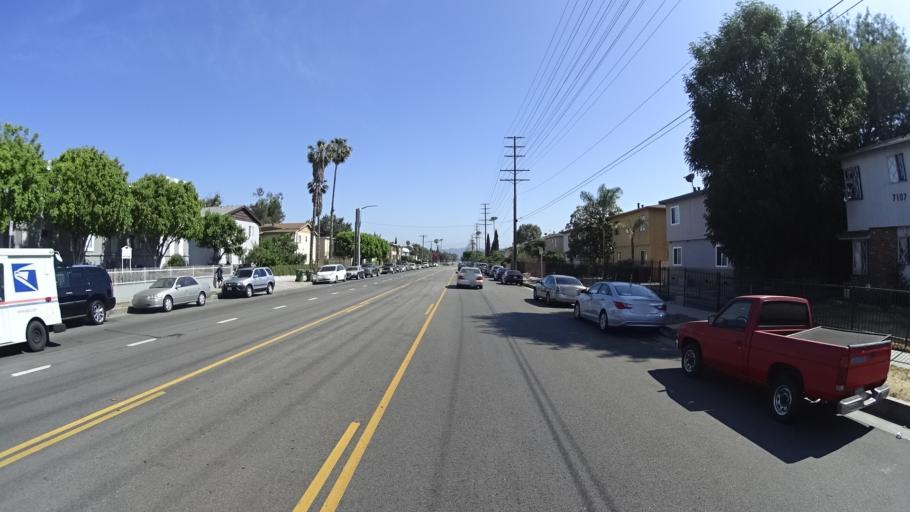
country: US
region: California
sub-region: Los Angeles County
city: Van Nuys
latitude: 34.1997
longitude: -118.4226
